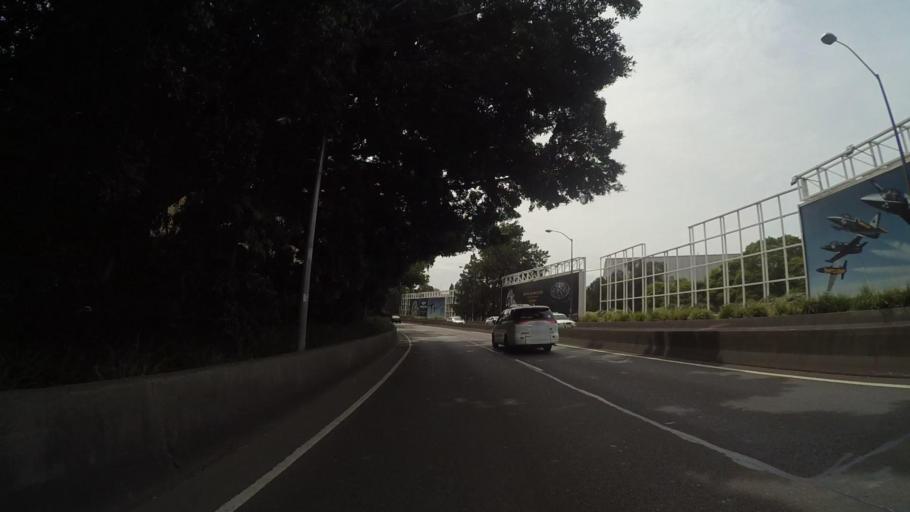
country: AU
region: New South Wales
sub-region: Botany Bay
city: Mascot
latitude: -33.9277
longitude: 151.1837
